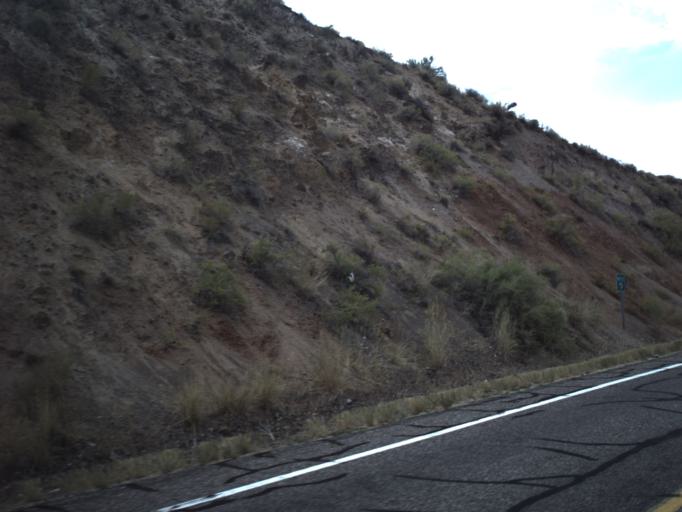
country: US
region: Utah
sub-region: Sevier County
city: Richfield
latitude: 38.7681
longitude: -111.9792
